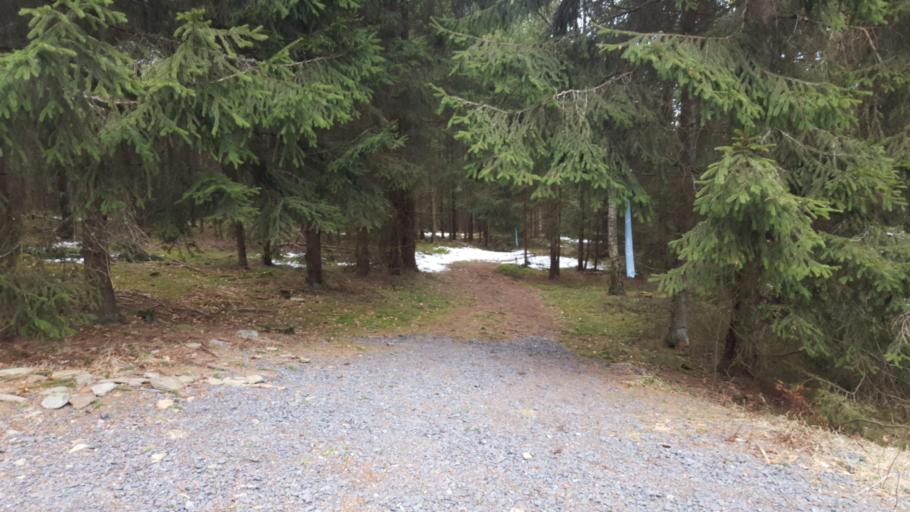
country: CZ
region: Karlovarsky
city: As
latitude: 50.2365
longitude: 12.2051
